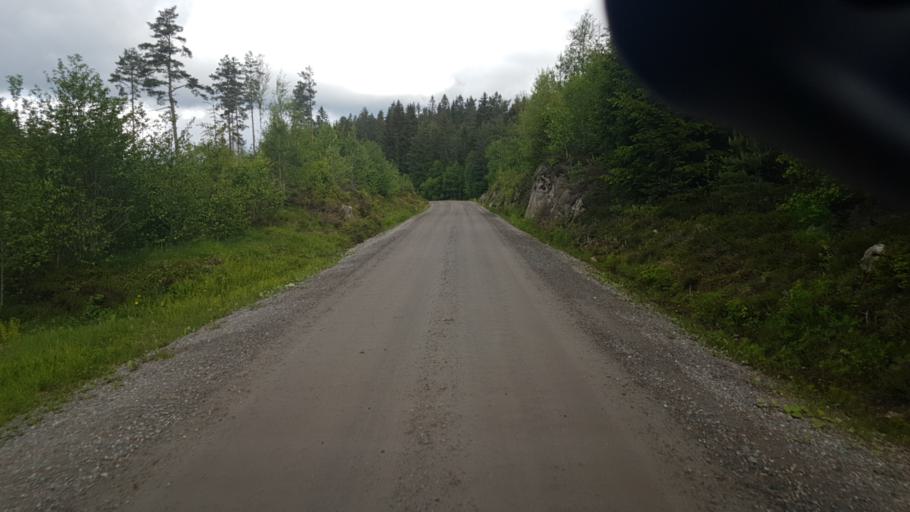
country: NO
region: Ostfold
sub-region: Romskog
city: Romskog
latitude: 59.7069
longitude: 12.0459
